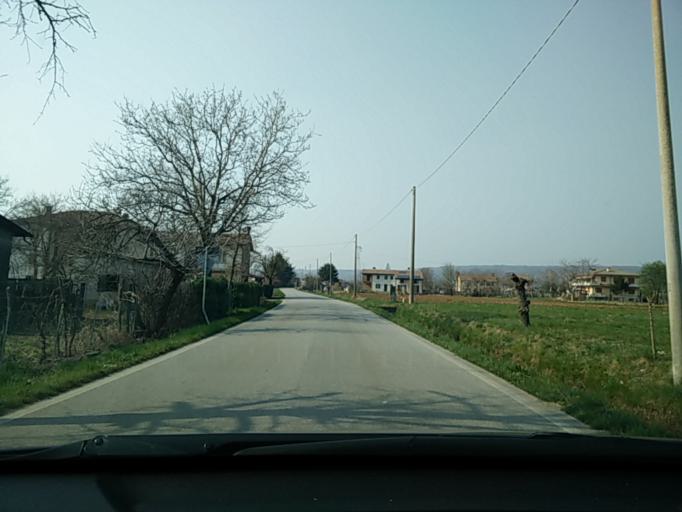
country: IT
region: Veneto
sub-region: Provincia di Treviso
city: Falze-Signoressa
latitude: 45.7585
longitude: 12.1198
